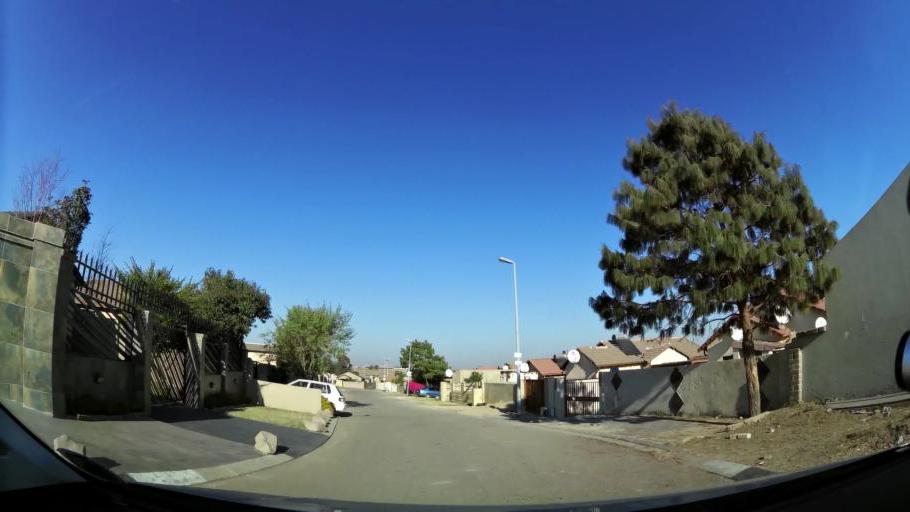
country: ZA
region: Gauteng
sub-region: City of Johannesburg Metropolitan Municipality
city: Modderfontein
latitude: -26.0442
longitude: 28.1615
